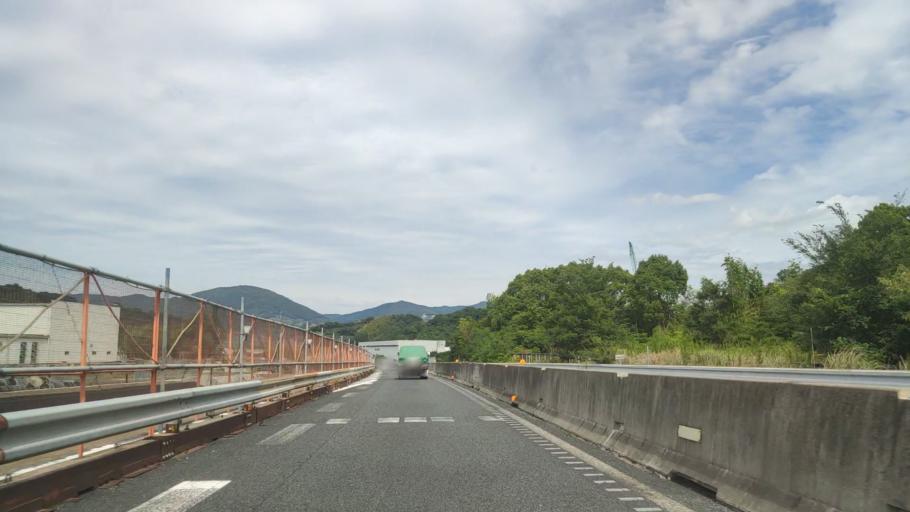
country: JP
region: Wakayama
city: Kainan
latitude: 34.0415
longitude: 135.2032
